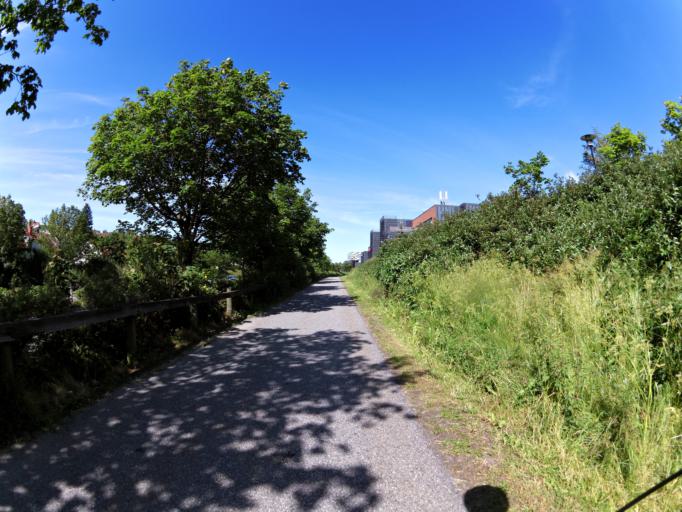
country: NO
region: Ostfold
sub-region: Fredrikstad
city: Fredrikstad
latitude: 59.2217
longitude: 10.9506
